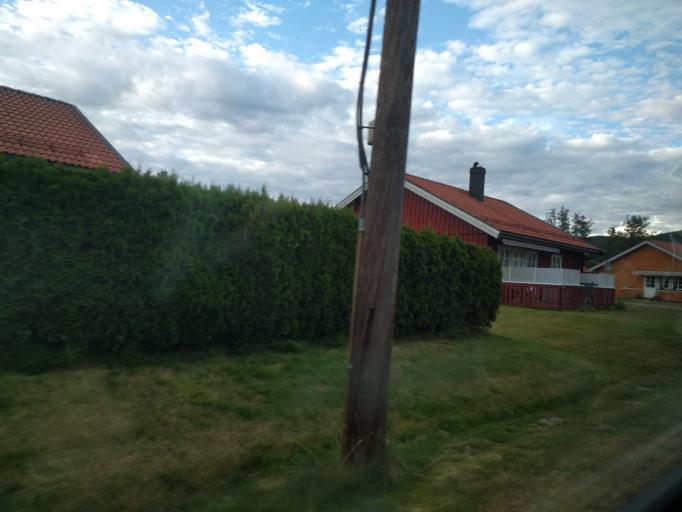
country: NO
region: Vestfold
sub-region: Lardal
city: Svarstad
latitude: 59.3126
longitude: 9.8840
